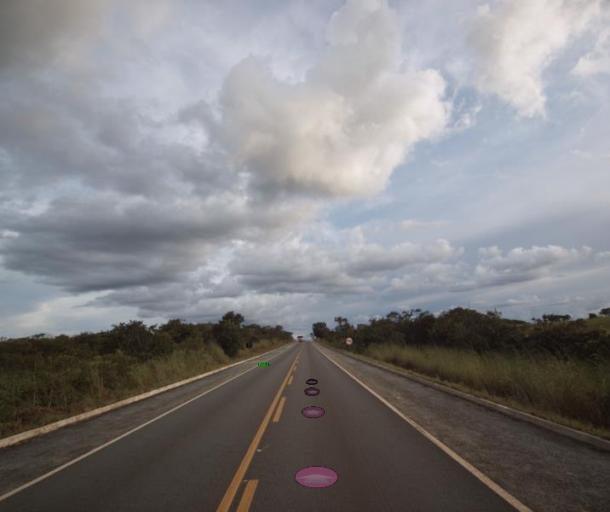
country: BR
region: Goias
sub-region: Barro Alto
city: Barro Alto
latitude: -14.8896
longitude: -48.6411
